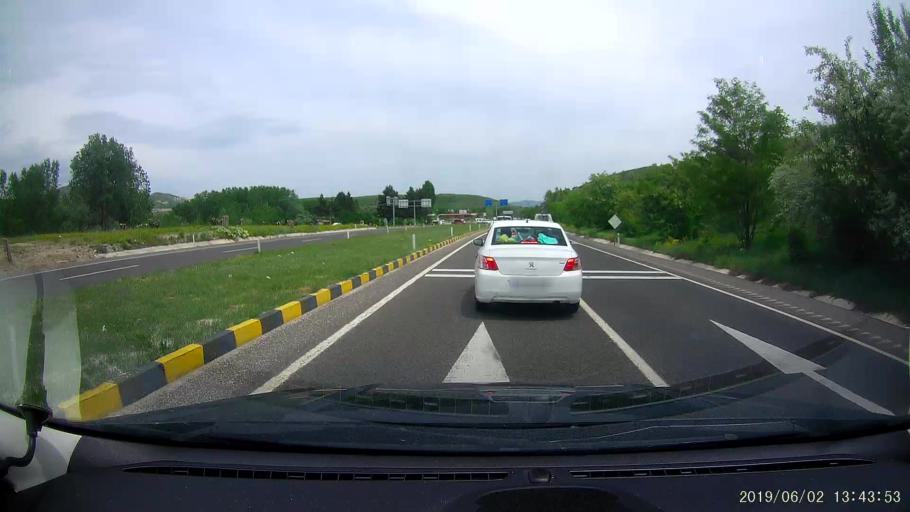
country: TR
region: Cankiri
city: Kursunlu
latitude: 40.8492
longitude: 33.2252
